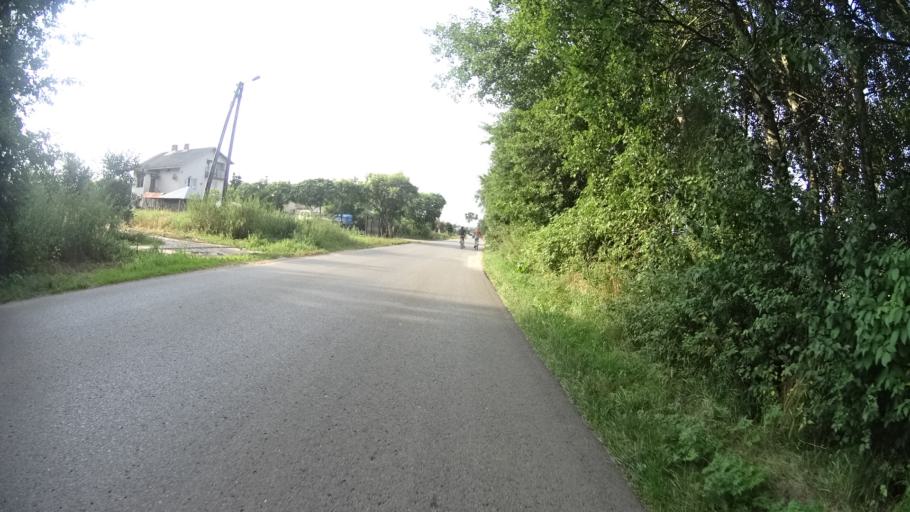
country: PL
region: Masovian Voivodeship
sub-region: Powiat grojecki
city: Mogielnica
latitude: 51.6818
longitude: 20.7321
